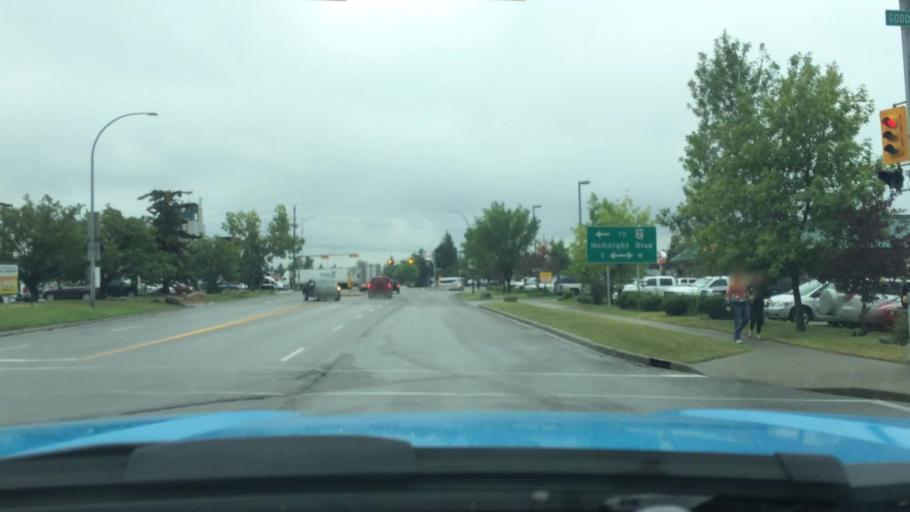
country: CA
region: Alberta
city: Calgary
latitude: 51.0976
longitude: -114.0540
